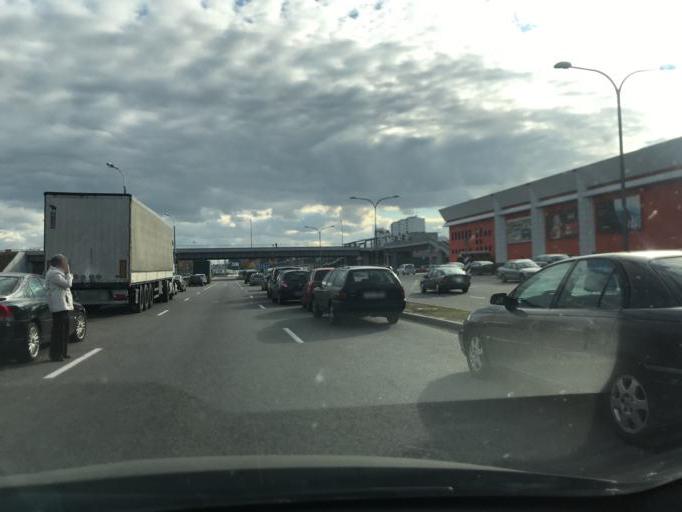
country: BY
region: Minsk
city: Borovlyany
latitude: 53.9366
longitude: 27.6743
